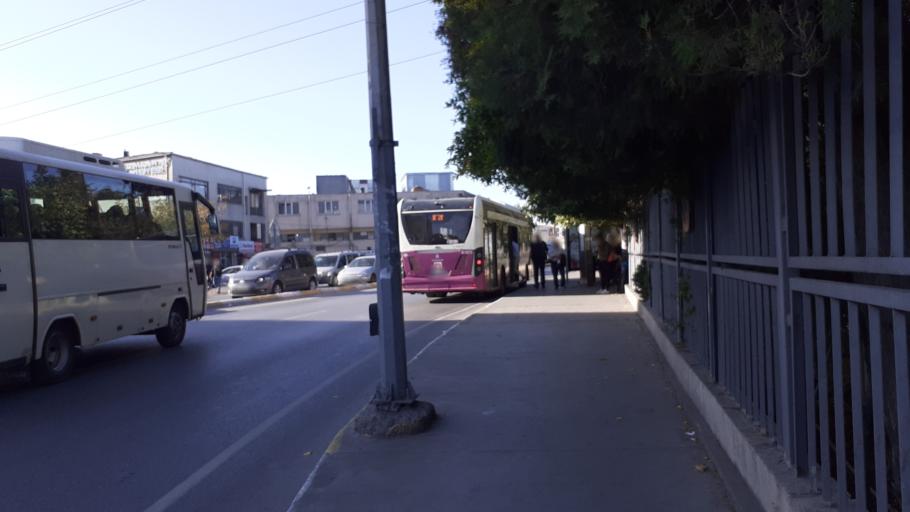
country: TR
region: Istanbul
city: Mahmutbey
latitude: 41.0106
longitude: 28.7935
